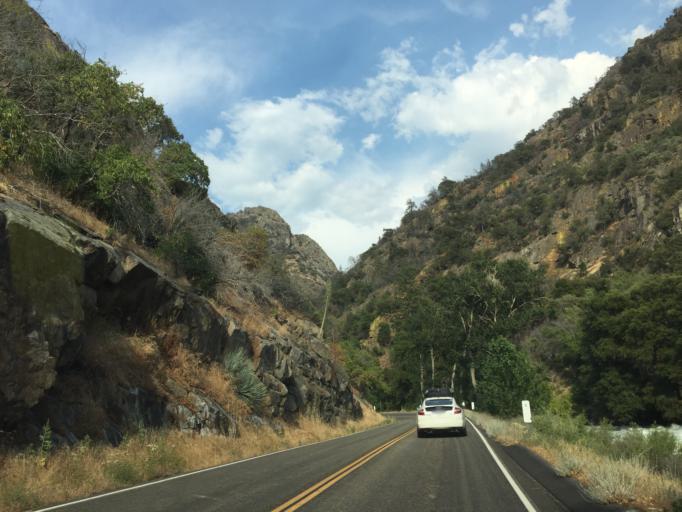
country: US
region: California
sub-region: Tulare County
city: Three Rivers
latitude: 36.8081
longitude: -118.7944
